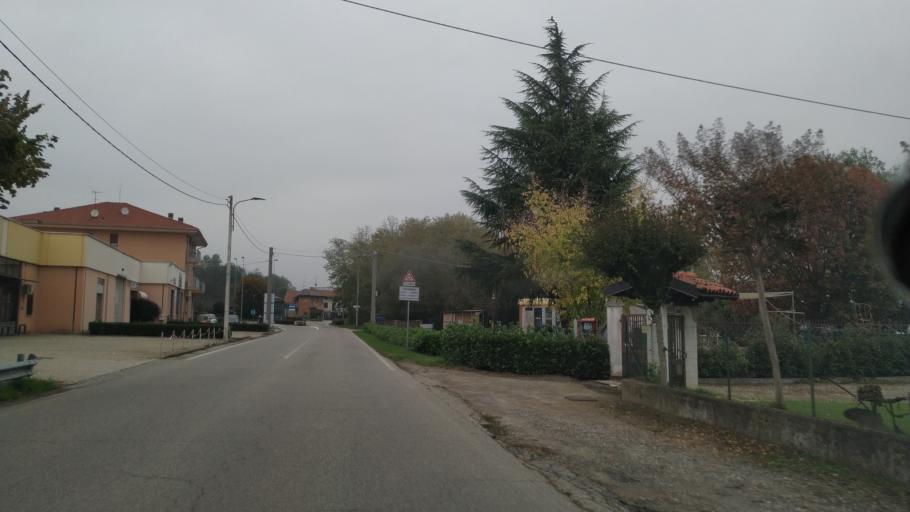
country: IT
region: Piedmont
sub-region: Provincia di Biella
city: Cerreto Castello
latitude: 45.5576
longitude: 8.1713
